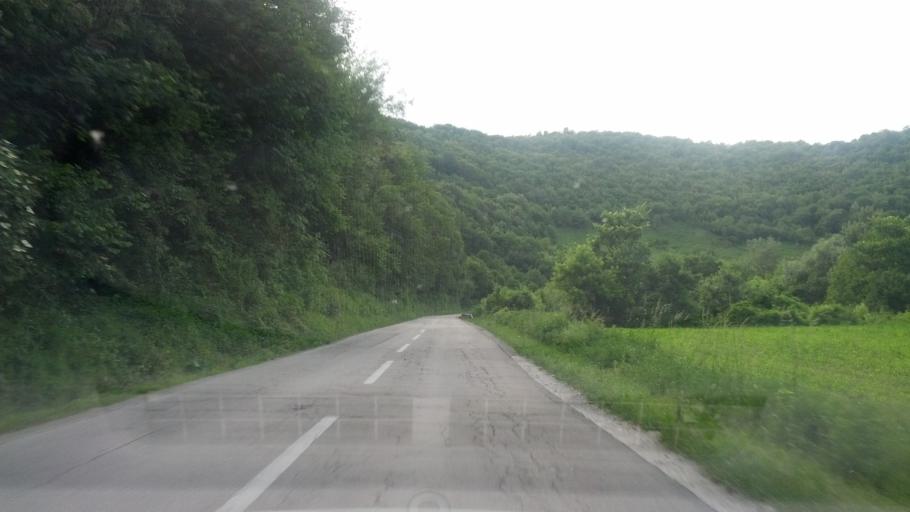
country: BA
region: Federation of Bosnia and Herzegovina
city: Stijena
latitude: 44.9021
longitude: 15.9952
